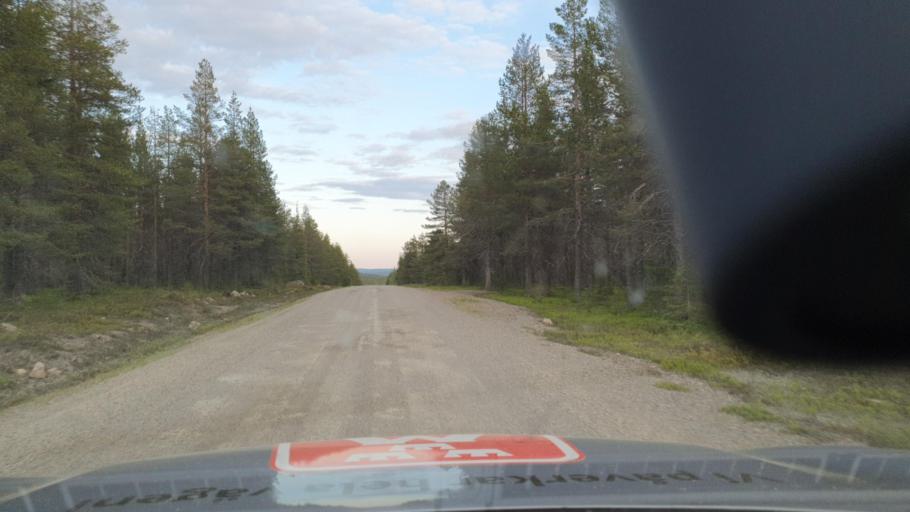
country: SE
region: Norrbotten
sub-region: Gallivare Kommun
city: Gaellivare
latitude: 66.6203
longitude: 21.3464
